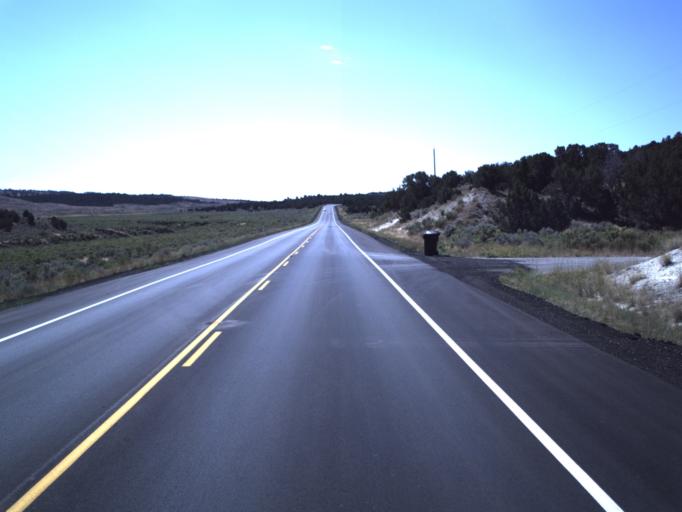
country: US
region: Utah
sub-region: Utah County
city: Eagle Mountain
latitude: 40.0197
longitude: -112.2798
